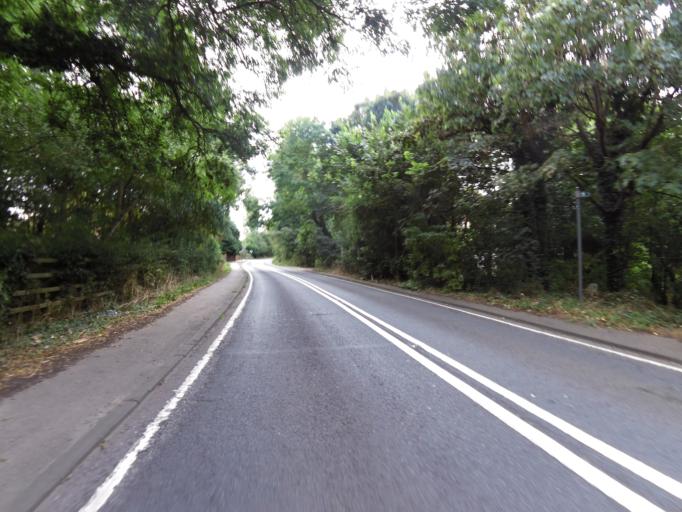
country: GB
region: England
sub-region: Hertfordshire
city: Shenley AV
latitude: 51.7153
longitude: -0.2998
